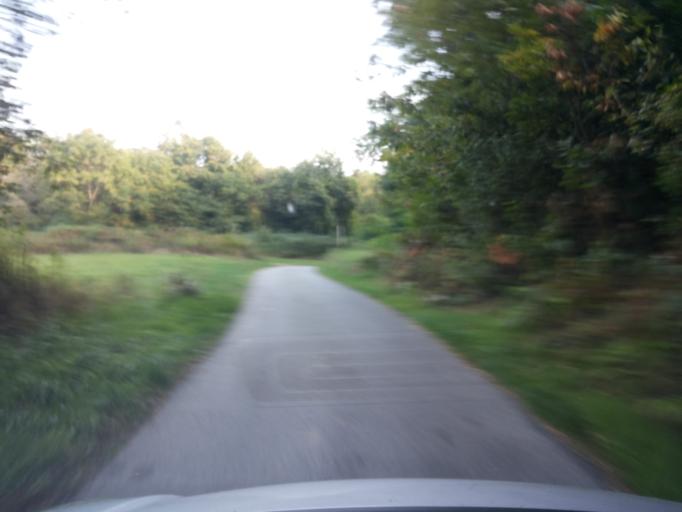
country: IT
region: Piedmont
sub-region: Provincia di Biella
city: Roppolo
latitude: 45.4223
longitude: 8.0826
